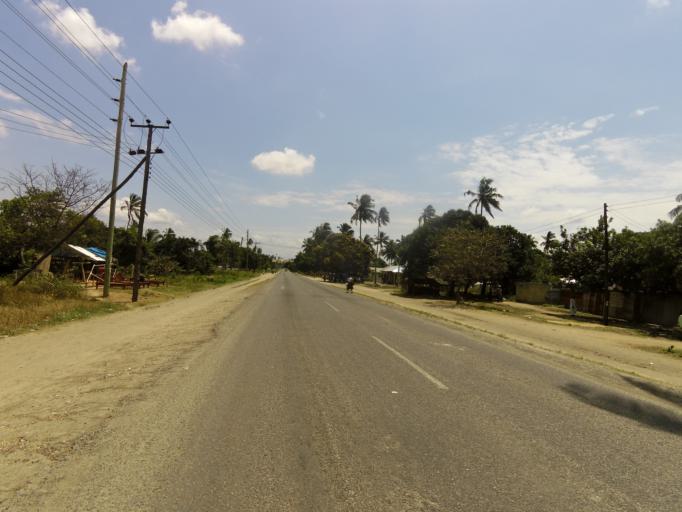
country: TZ
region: Pwani
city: Vikindu
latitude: -7.0331
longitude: 39.2805
